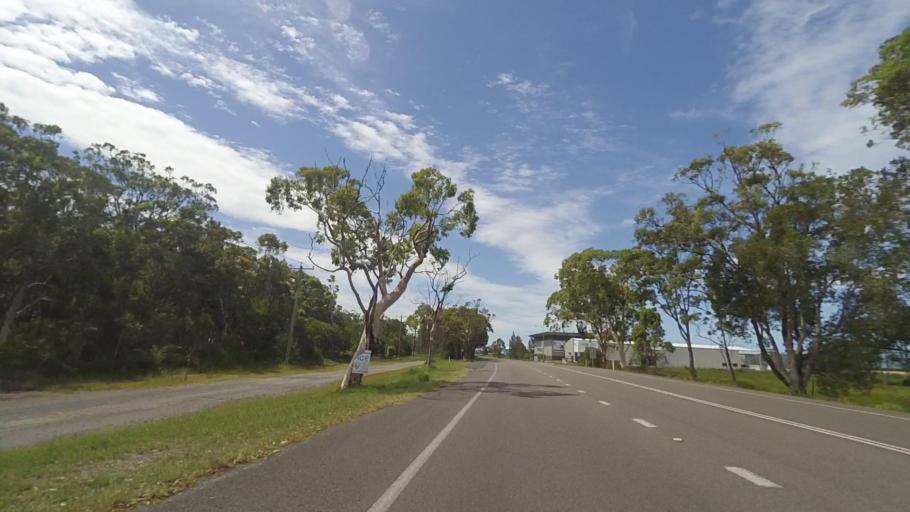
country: AU
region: New South Wales
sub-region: Port Stephens Shire
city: Anna Bay
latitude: -32.7543
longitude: 152.0684
